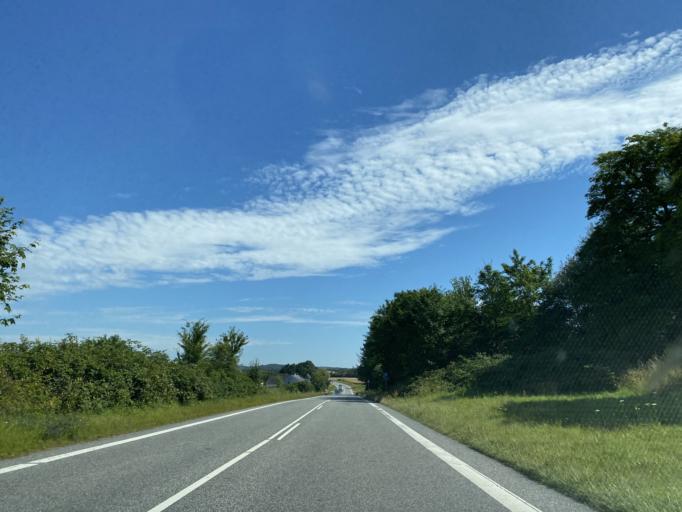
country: DK
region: South Denmark
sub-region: Faaborg-Midtfyn Kommune
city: Faaborg
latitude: 55.1087
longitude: 10.1928
